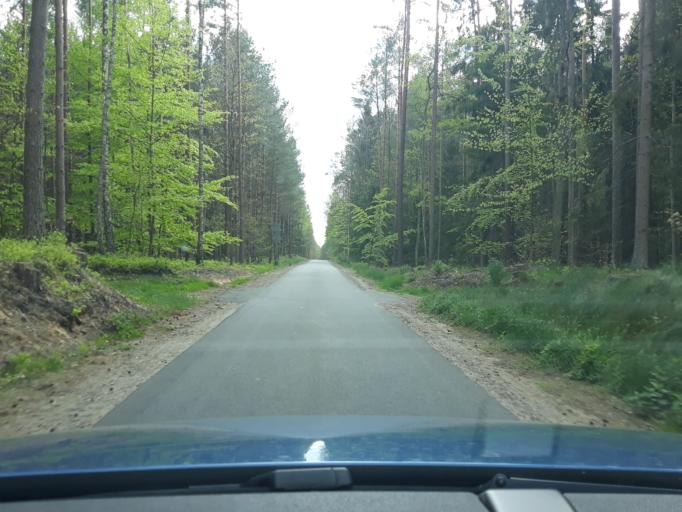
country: PL
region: Pomeranian Voivodeship
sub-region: Powiat czluchowski
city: Czluchow
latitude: 53.7413
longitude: 17.3487
